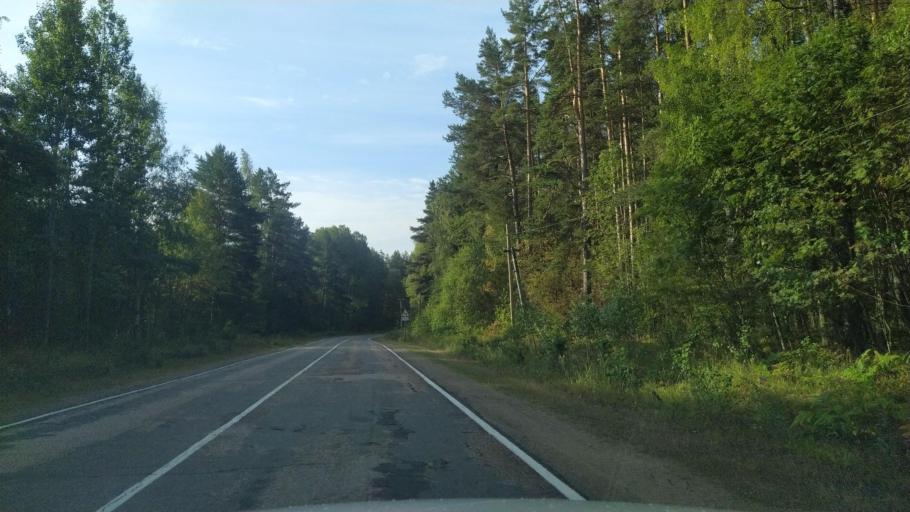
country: RU
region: Leningrad
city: Priozersk
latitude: 60.9939
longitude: 30.2554
